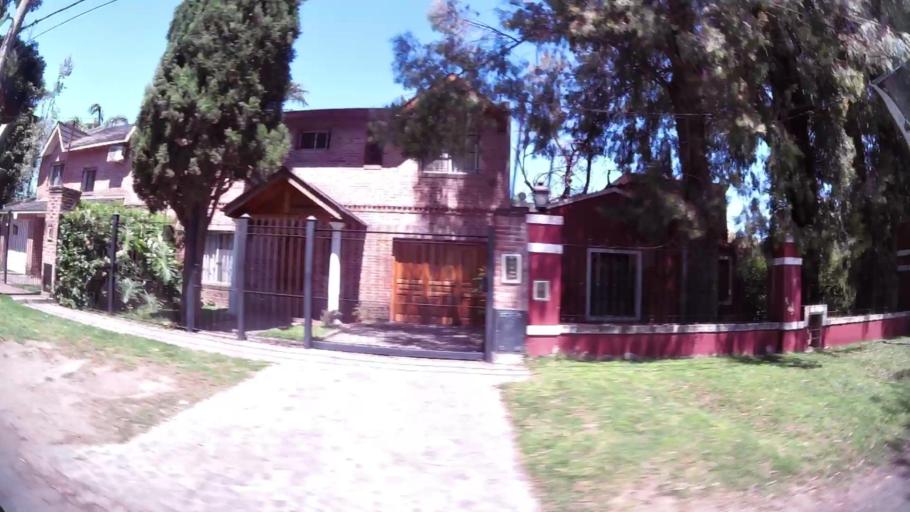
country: AR
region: Buenos Aires
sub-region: Partido de Tigre
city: Tigre
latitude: -34.4902
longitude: -58.6322
